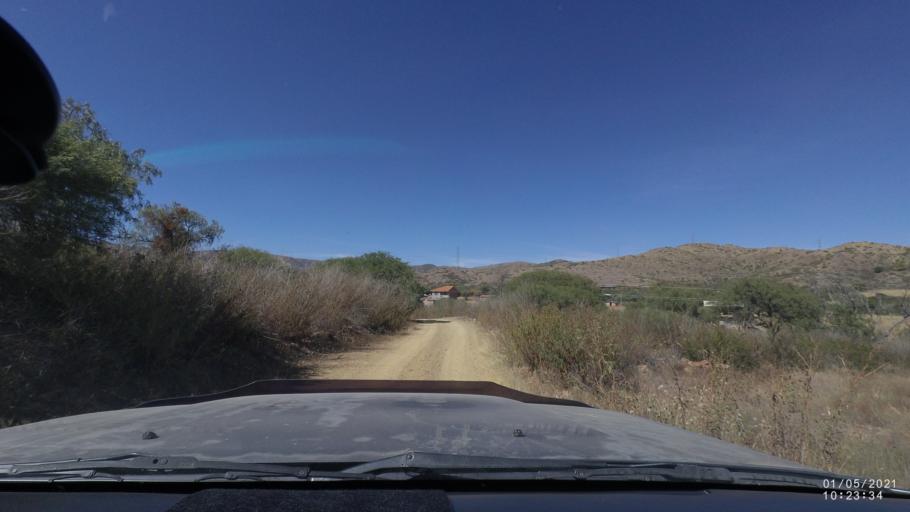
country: BO
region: Cochabamba
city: Capinota
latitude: -17.5722
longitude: -66.1961
